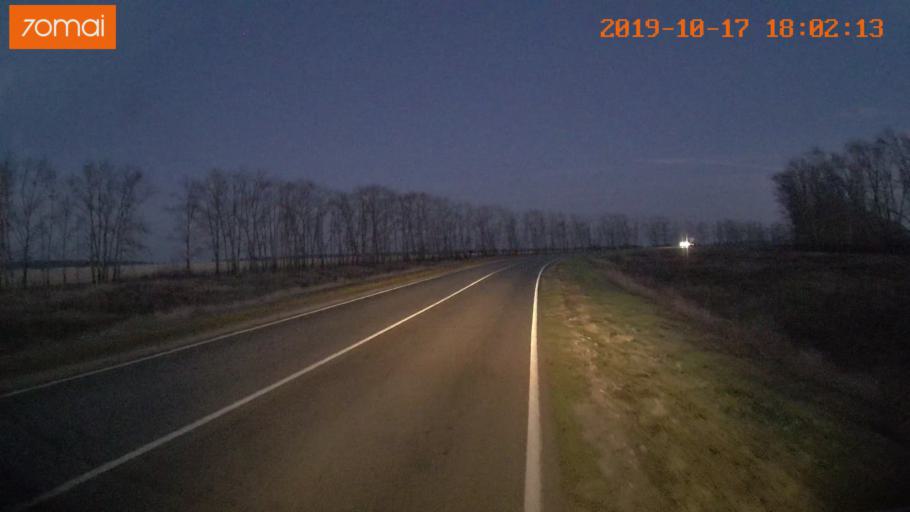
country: RU
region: Tula
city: Kurkino
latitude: 53.5071
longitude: 38.6119
